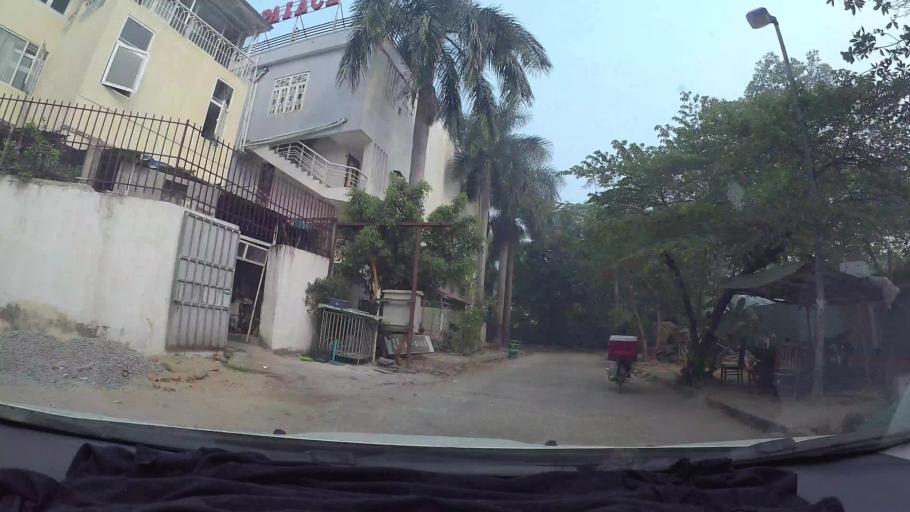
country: VN
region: Da Nang
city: Son Tra
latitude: 16.0487
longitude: 108.2250
